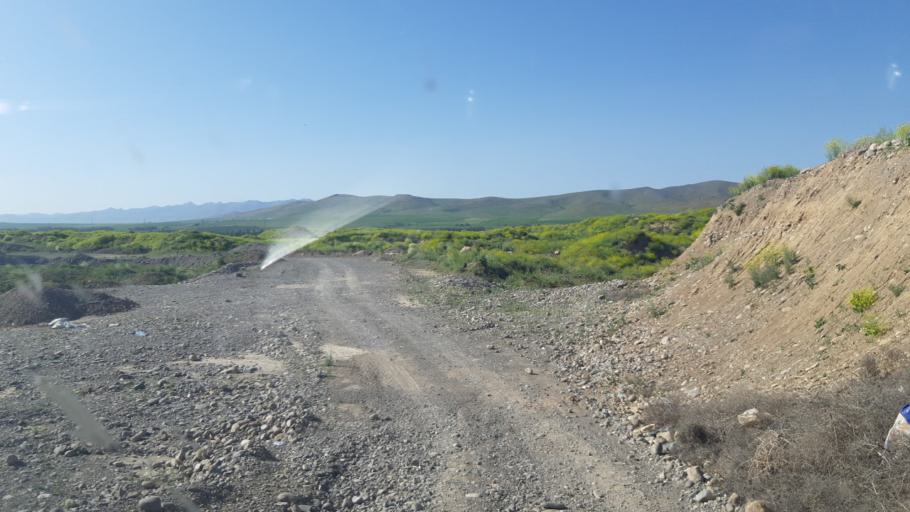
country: KZ
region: Ongtustik Qazaqstan
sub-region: Tulkibas Audany
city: Zhabagly
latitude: 42.5087
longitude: 70.4647
